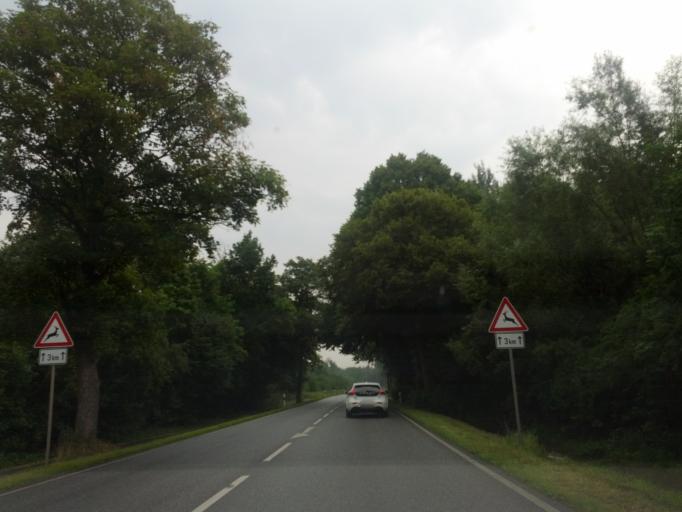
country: DE
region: Mecklenburg-Vorpommern
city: Bad Doberan
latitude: 54.1063
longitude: 11.9320
